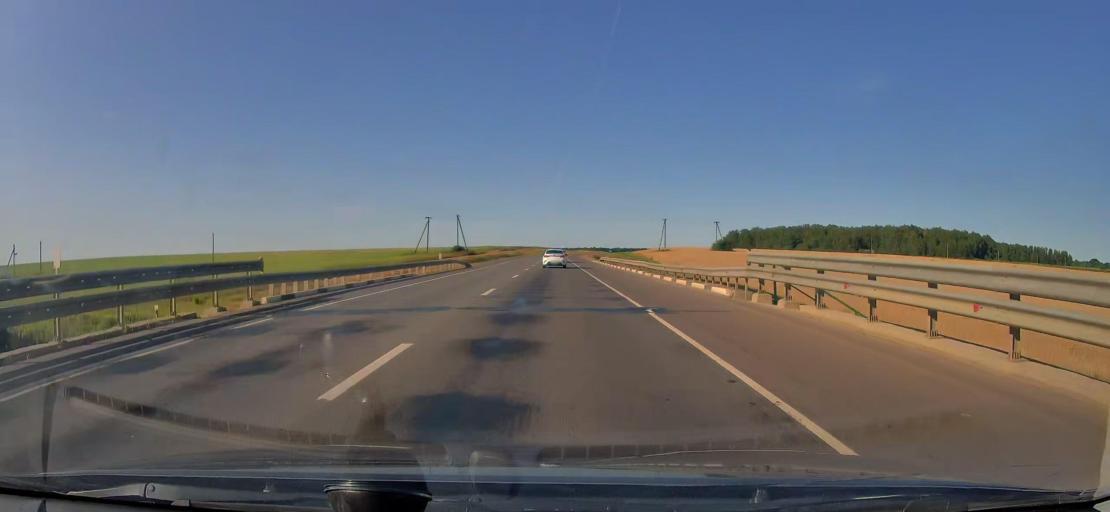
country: RU
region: Orjol
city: Spasskoye-Lutovinovo
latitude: 53.3183
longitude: 36.7003
